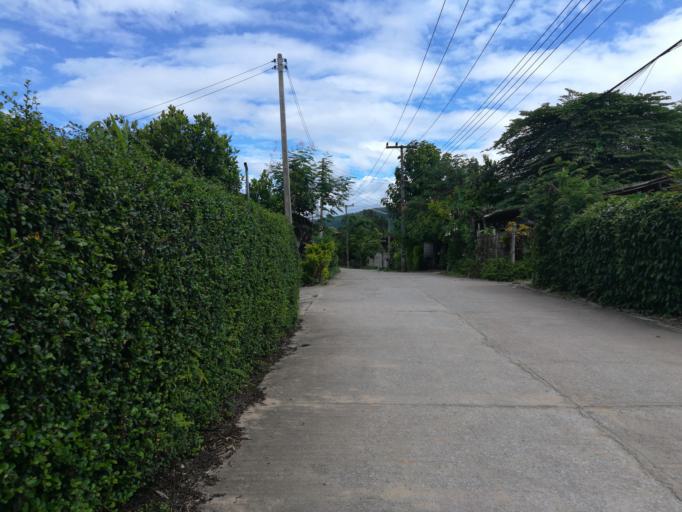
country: TH
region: Chiang Mai
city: Chom Thong
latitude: 18.4066
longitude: 98.6496
